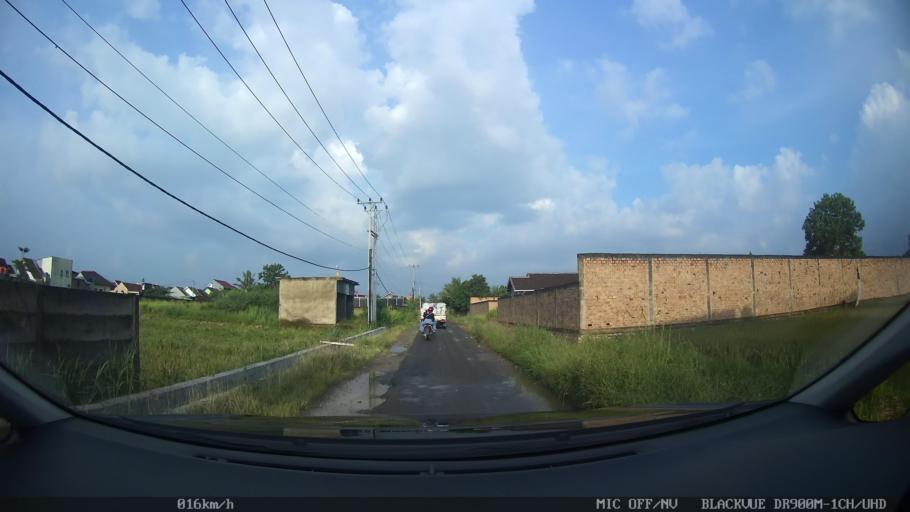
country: ID
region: Lampung
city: Kedaton
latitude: -5.3908
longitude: 105.3127
